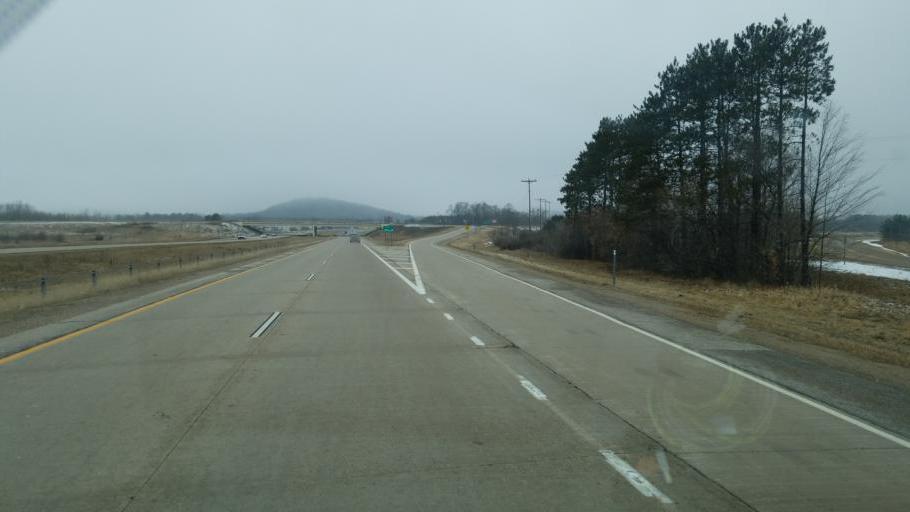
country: US
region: Wisconsin
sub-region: Waupaca County
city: Waupaca
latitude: 44.3297
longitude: -89.0364
